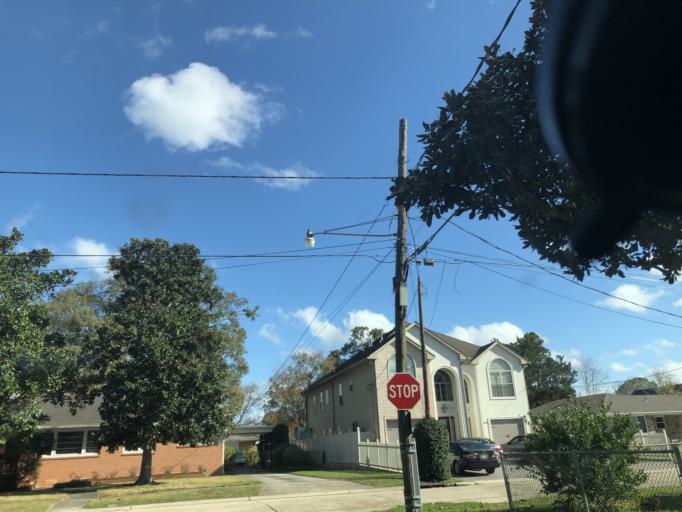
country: US
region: Louisiana
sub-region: Jefferson Parish
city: Metairie Terrace
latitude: 29.9829
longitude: -90.1594
